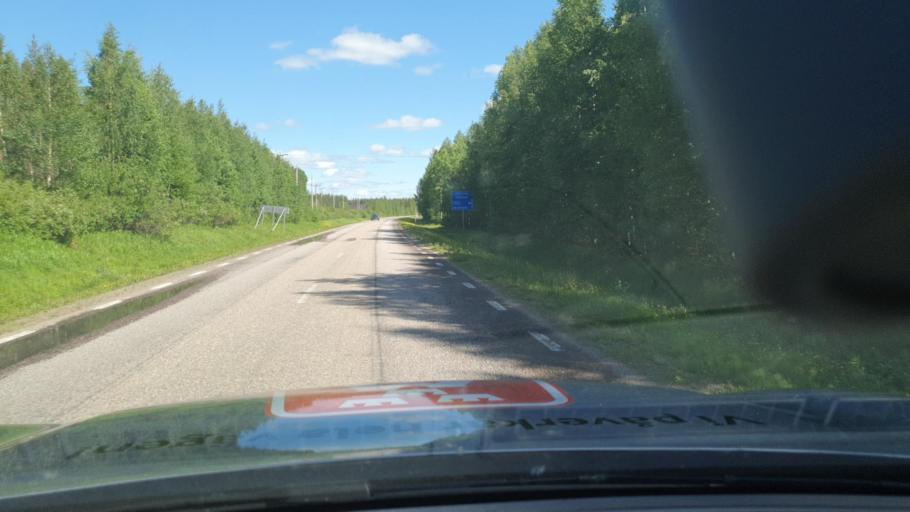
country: SE
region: Norrbotten
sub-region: Overkalix Kommun
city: OEverkalix
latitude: 67.0680
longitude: 22.5191
